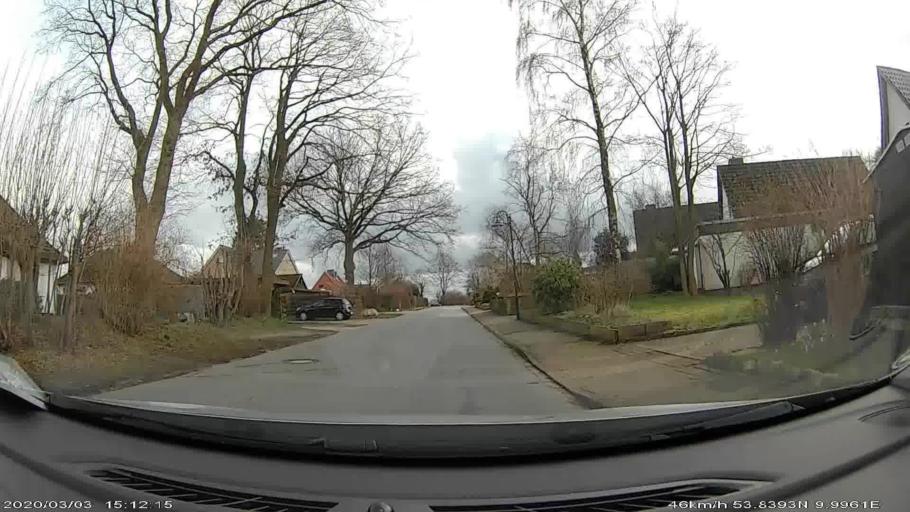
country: DE
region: Schleswig-Holstein
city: Oersdorf
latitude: 53.8397
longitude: 9.9958
